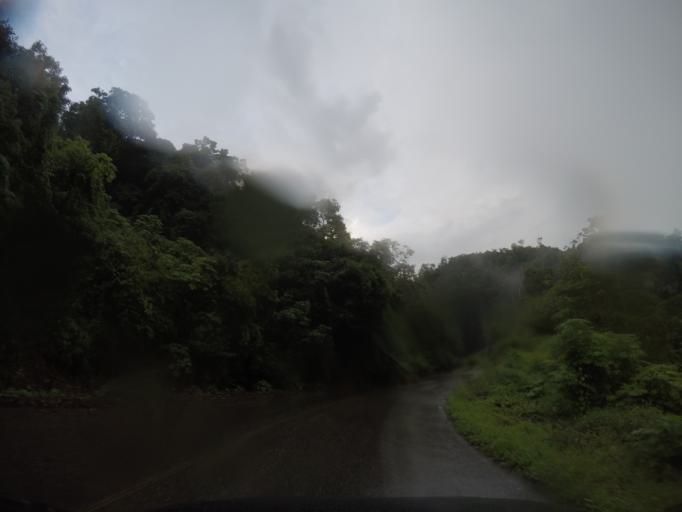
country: MX
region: Oaxaca
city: San Gabriel Mixtepec
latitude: 16.0682
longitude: -97.0755
